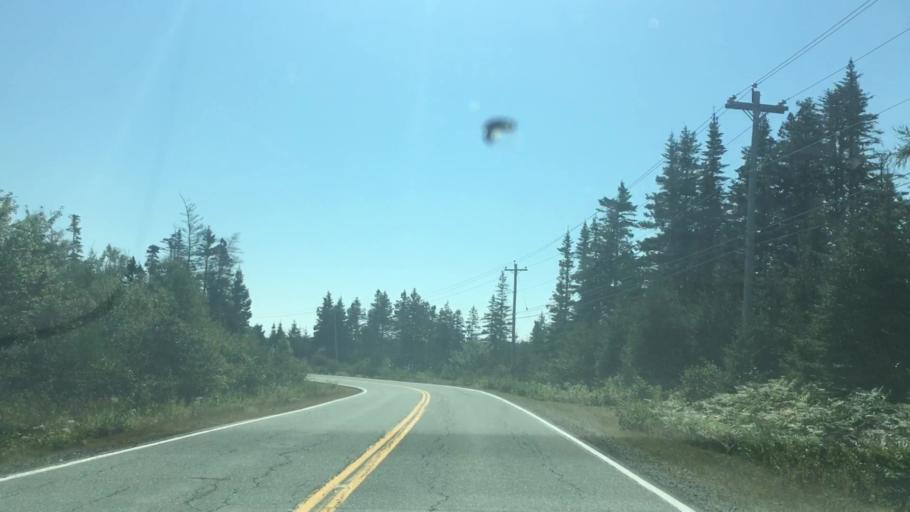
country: CA
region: Nova Scotia
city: Antigonish
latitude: 45.0085
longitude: -62.0902
